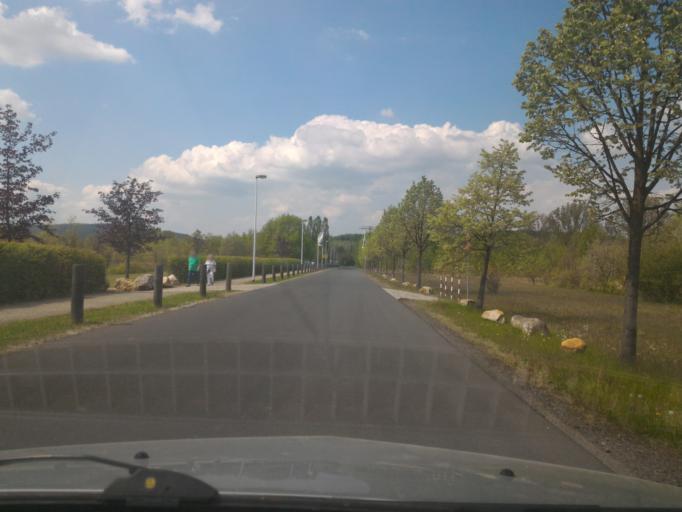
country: DE
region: Saxony
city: Olbersdorf
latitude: 50.8957
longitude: 14.7705
